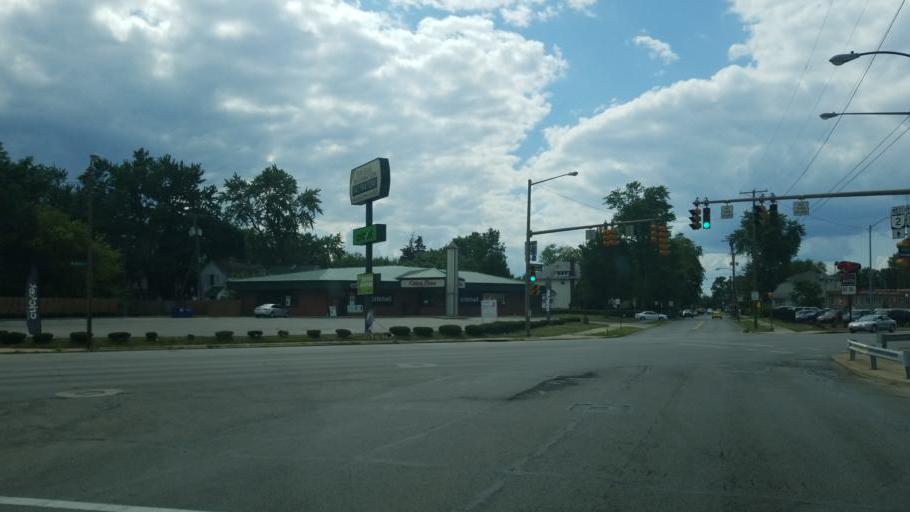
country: US
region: Ohio
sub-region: Lucas County
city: Oregon
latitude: 41.6363
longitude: -83.5179
